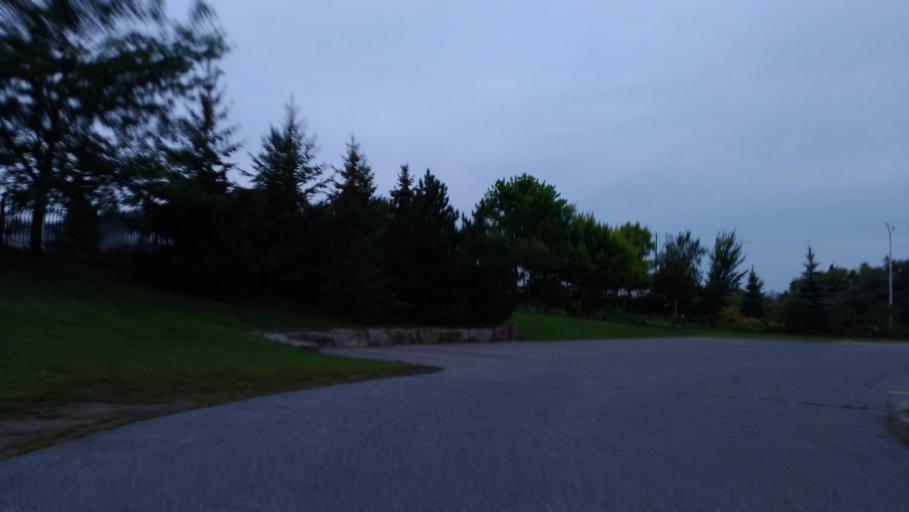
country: CA
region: Ontario
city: Bells Corners
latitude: 45.3553
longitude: -75.9342
